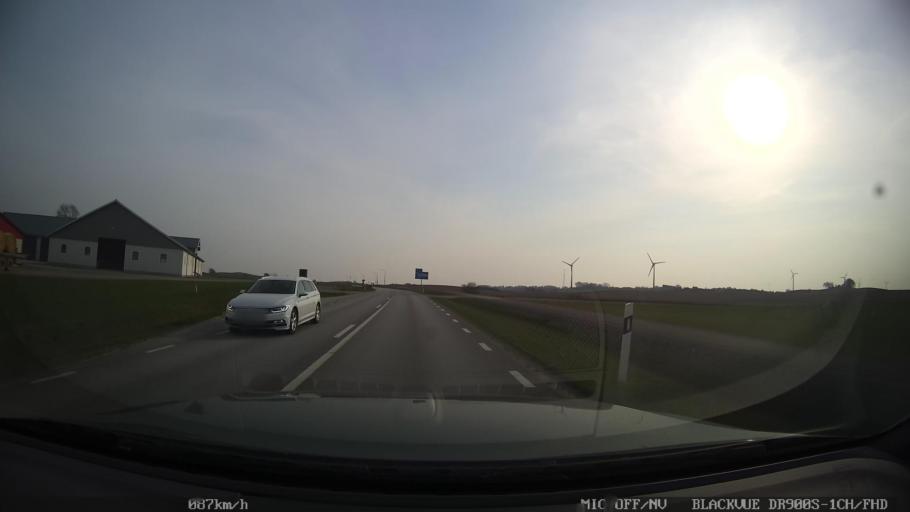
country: SE
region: Skane
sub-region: Ystads Kommun
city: Ystad
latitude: 55.4714
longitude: 13.7973
